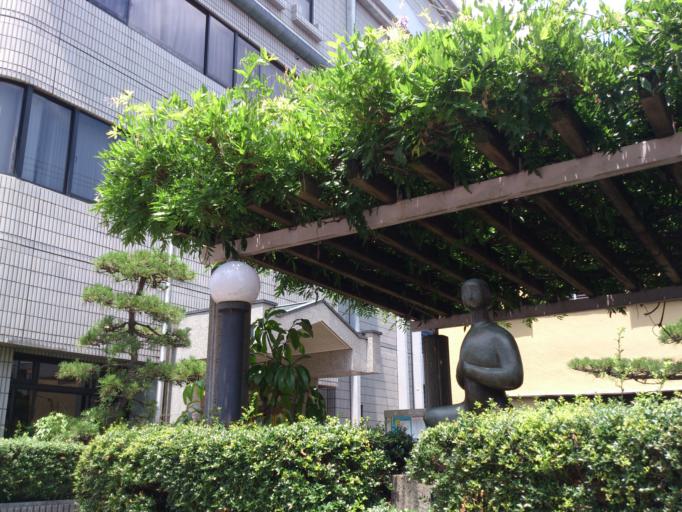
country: JP
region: Chiba
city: Matsudo
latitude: 35.7309
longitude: 139.9069
